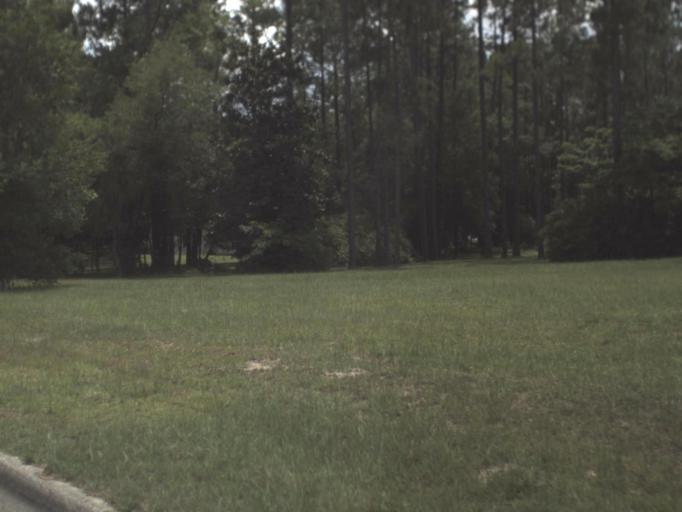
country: US
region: Florida
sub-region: Taylor County
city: Perry
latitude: 30.1032
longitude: -83.5595
